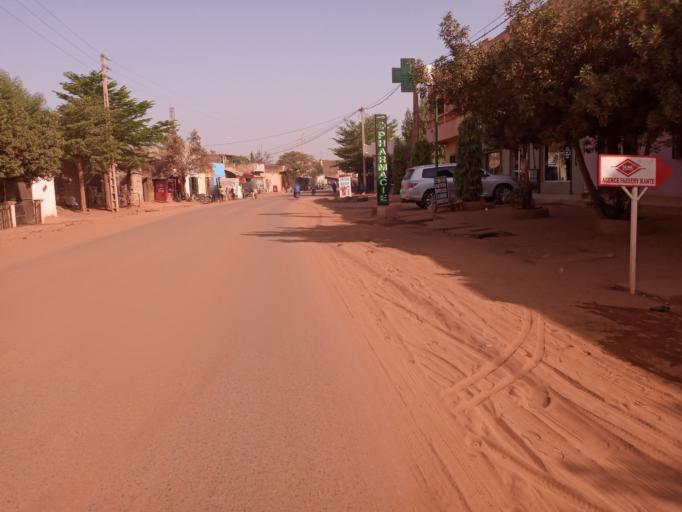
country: ML
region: Bamako
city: Bamako
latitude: 12.5797
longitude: -7.9573
